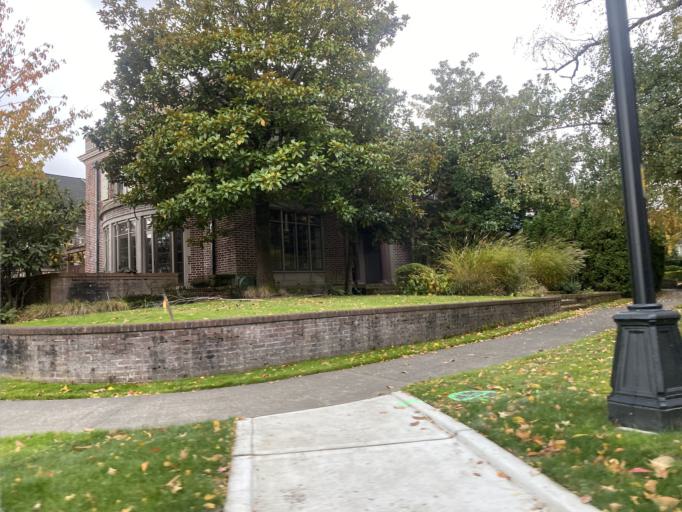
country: US
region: Washington
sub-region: King County
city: Seattle
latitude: 47.6463
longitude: -122.3016
